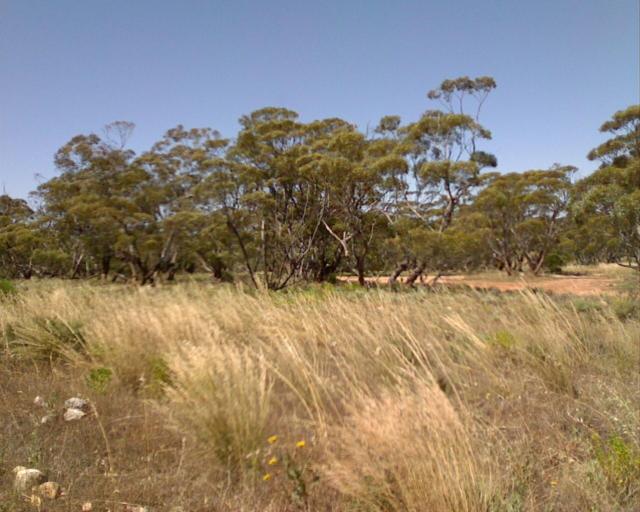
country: AU
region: South Australia
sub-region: Kimba
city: Caralue
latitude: -33.1339
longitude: 135.5518
